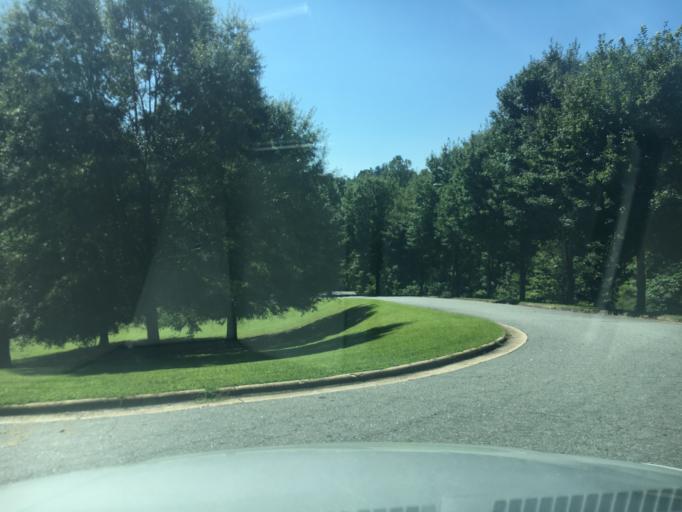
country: US
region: North Carolina
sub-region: McDowell County
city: West Marion
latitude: 35.6647
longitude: -82.0326
